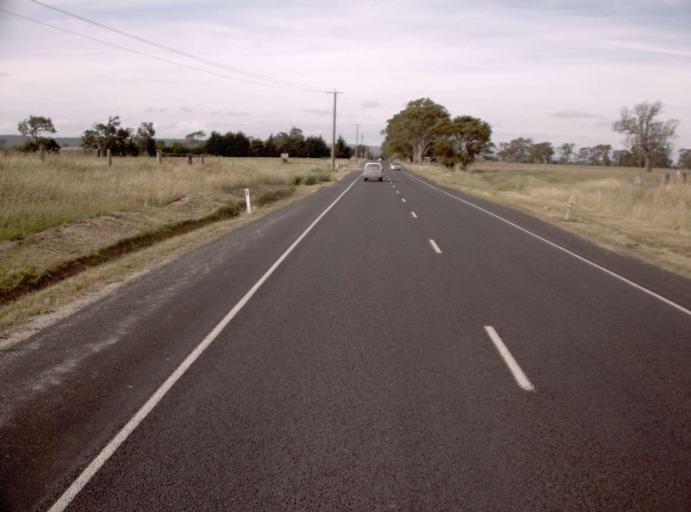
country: AU
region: Victoria
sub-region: Latrobe
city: Traralgon
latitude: -38.1486
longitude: 146.5549
